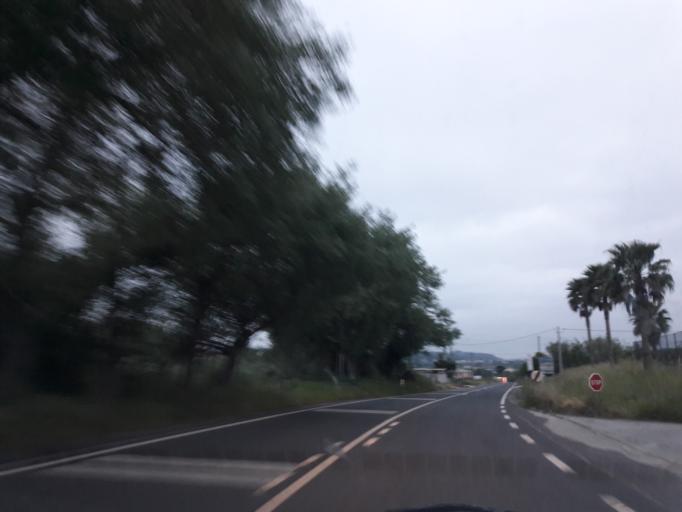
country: PT
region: Leiria
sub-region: Obidos
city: Obidos
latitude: 39.3737
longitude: -9.1398
